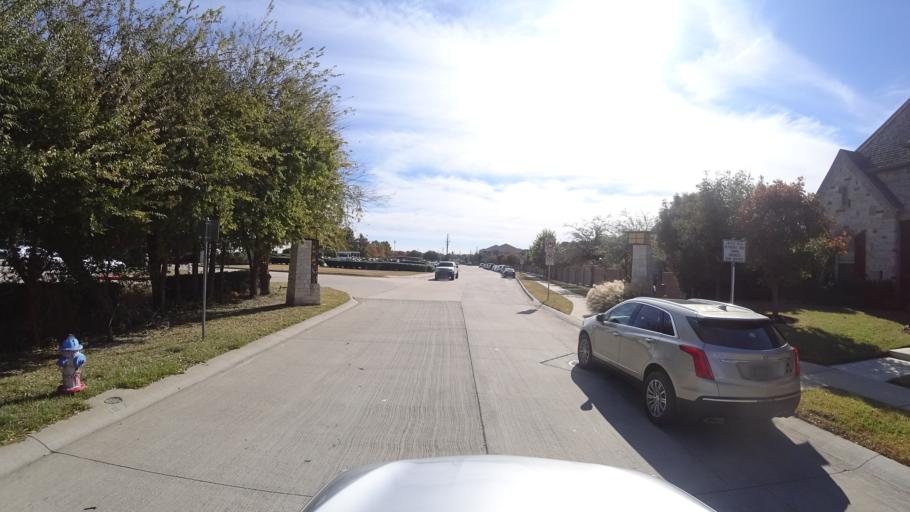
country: US
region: Texas
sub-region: Denton County
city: The Colony
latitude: 33.0292
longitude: -96.8872
